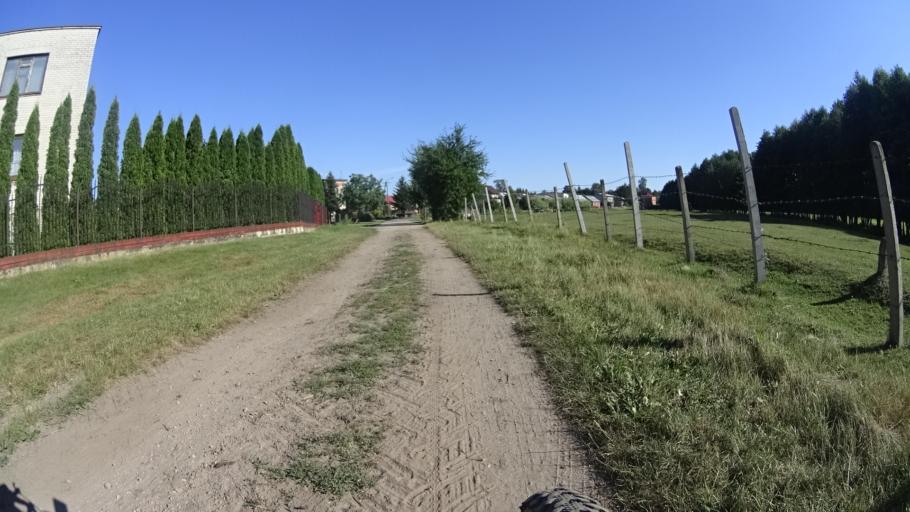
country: PL
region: Masovian Voivodeship
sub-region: Powiat bialobrzeski
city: Wysmierzyce
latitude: 51.6677
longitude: 20.8472
